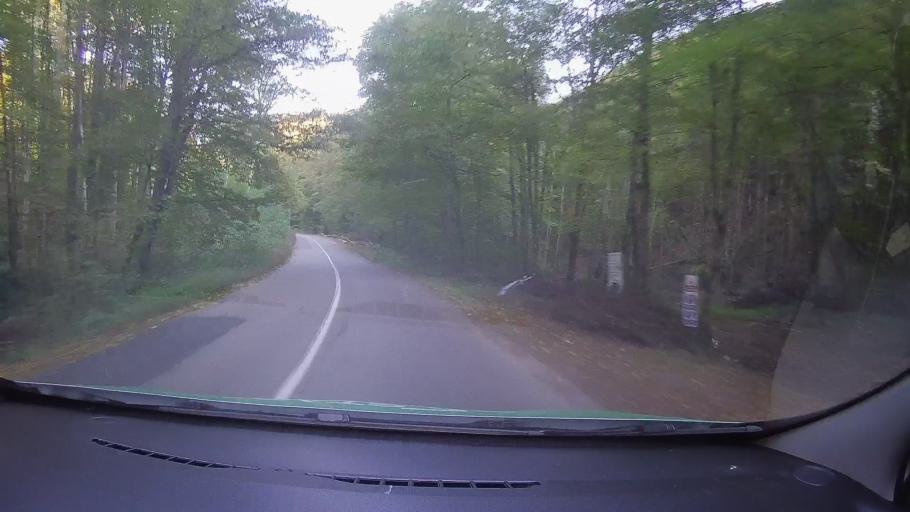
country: RO
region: Timis
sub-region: Comuna Nadrag
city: Nadrag
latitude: 45.6707
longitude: 22.1687
